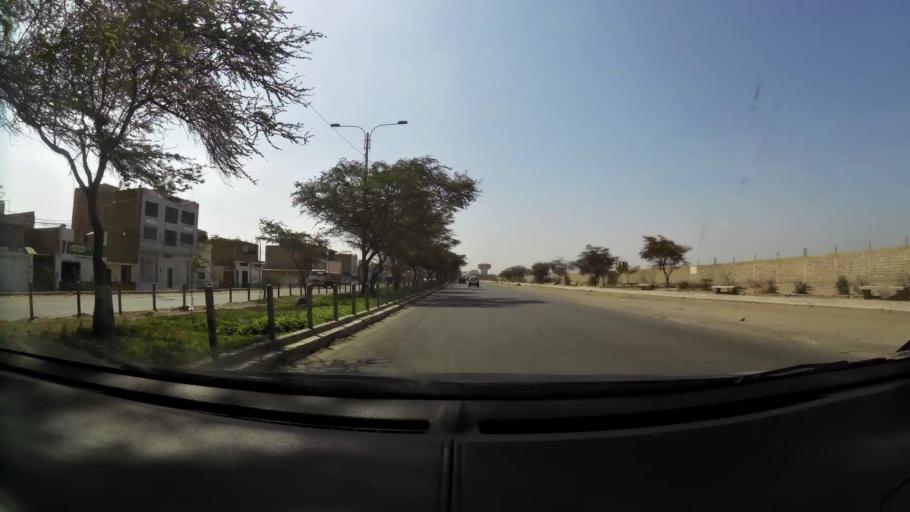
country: PE
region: Lambayeque
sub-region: Provincia de Chiclayo
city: Chiclayo
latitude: -6.7915
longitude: -79.8320
